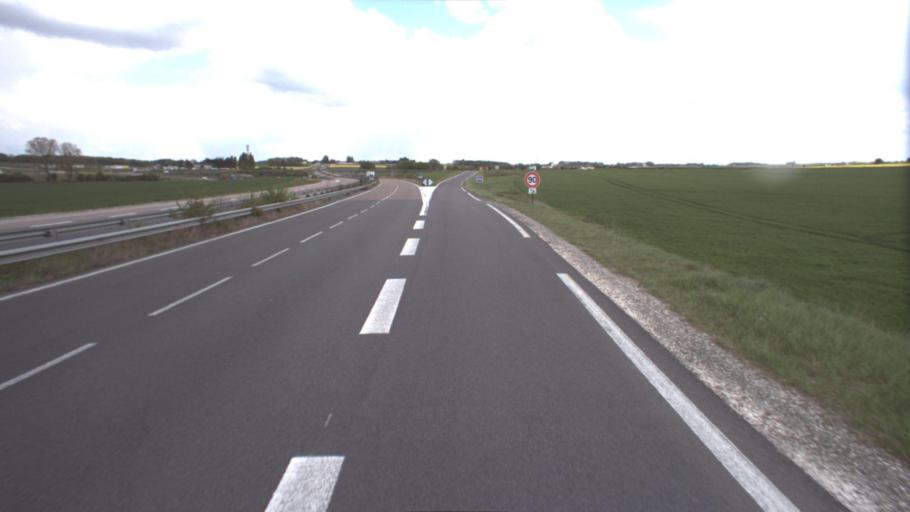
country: FR
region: Ile-de-France
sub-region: Departement de Seine-et-Marne
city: Jouy-le-Chatel
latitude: 48.6841
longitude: 3.0978
